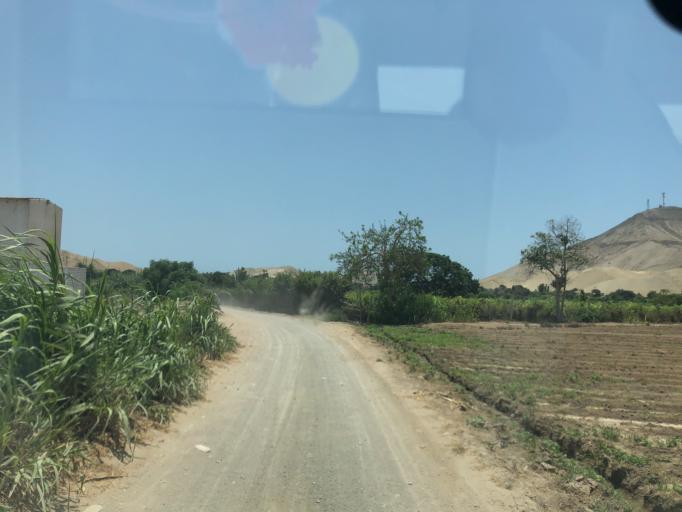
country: PE
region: Lima
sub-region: Provincia de Canete
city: Quilmana
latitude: -13.0000
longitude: -76.4473
